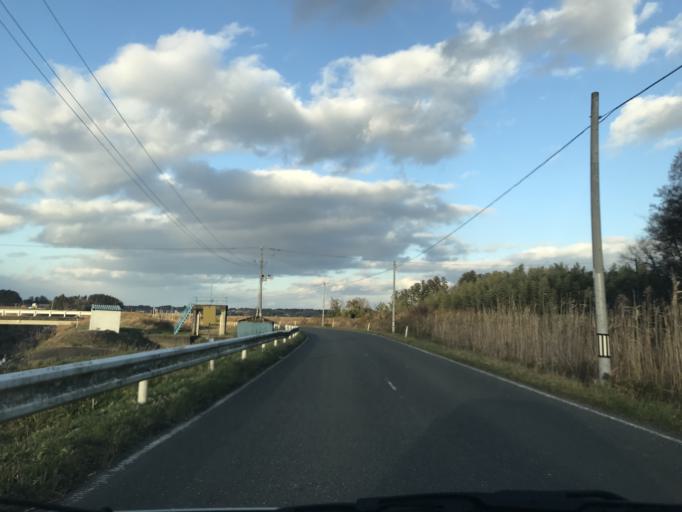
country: JP
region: Miyagi
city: Kogota
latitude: 38.6263
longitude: 141.0670
